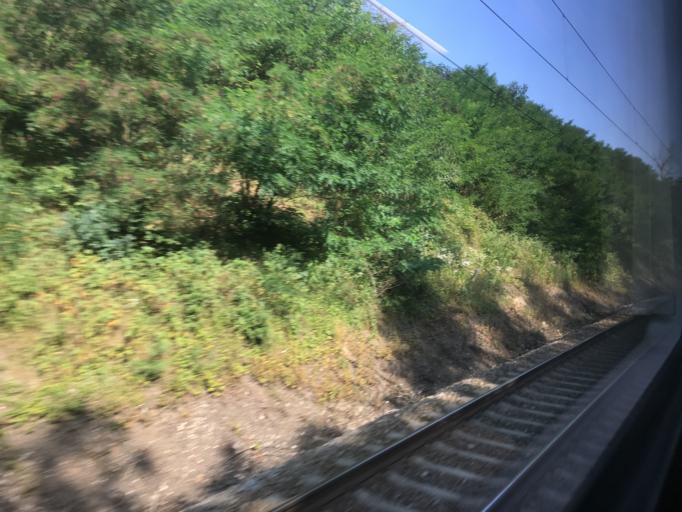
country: CZ
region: Central Bohemia
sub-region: Okres Benesov
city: Cercany
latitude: 49.8840
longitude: 14.7268
